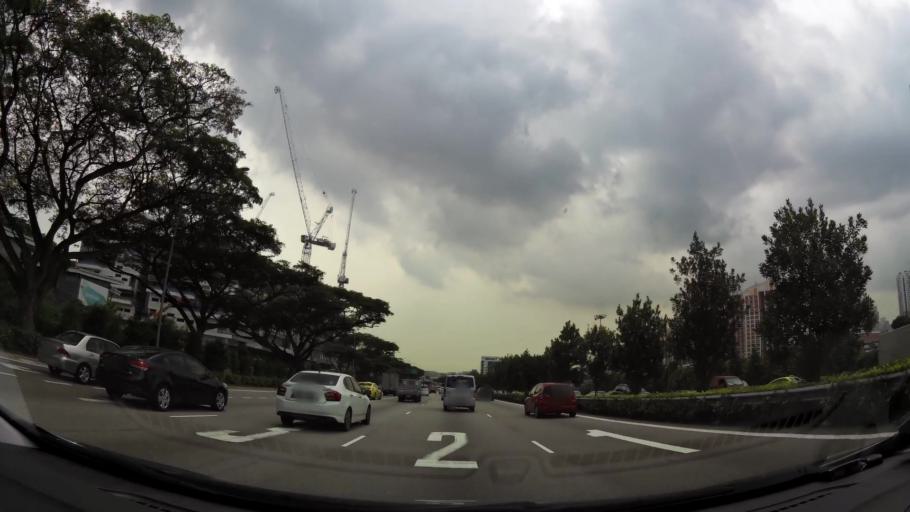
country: SG
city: Singapore
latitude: 1.3518
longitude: 103.8575
